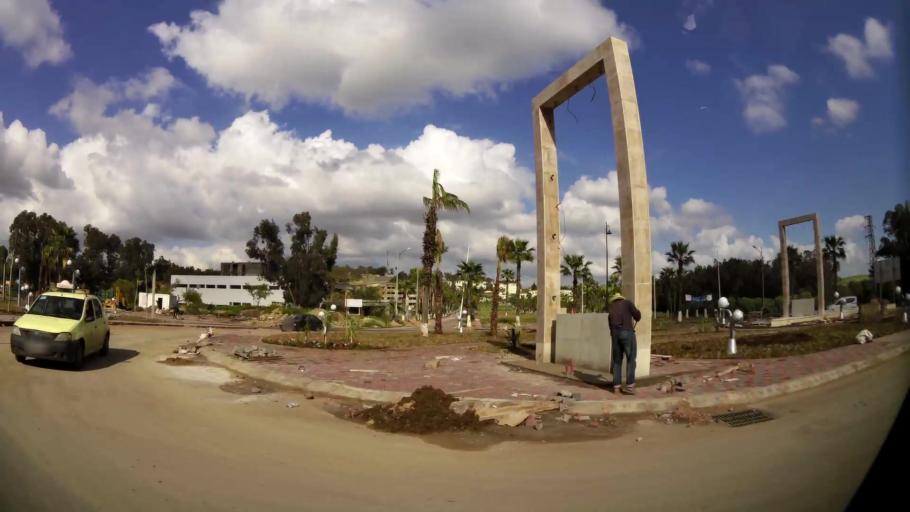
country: MA
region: Chaouia-Ouardigha
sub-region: Settat Province
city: Settat
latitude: 33.0327
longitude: -7.6229
